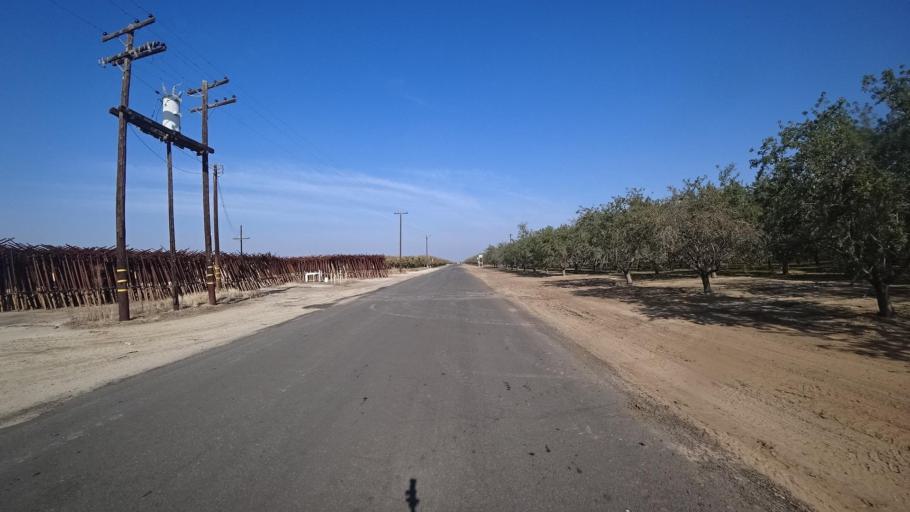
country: US
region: California
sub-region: Kern County
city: McFarland
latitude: 35.6516
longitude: -119.1868
